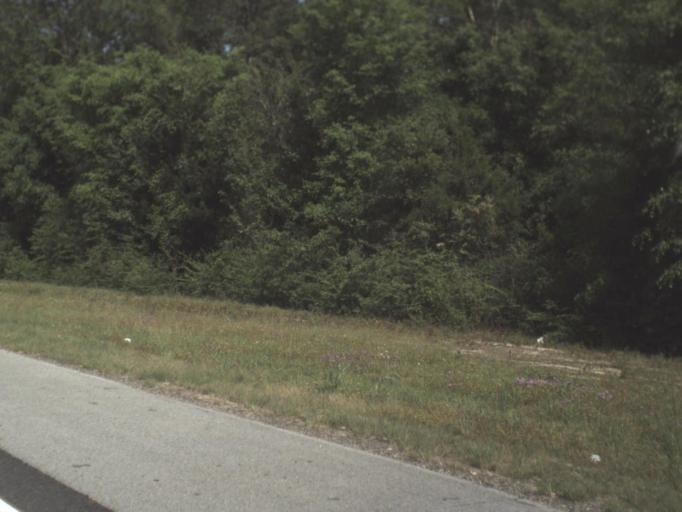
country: US
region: Florida
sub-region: Santa Rosa County
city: Bagdad
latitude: 30.5797
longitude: -87.0184
